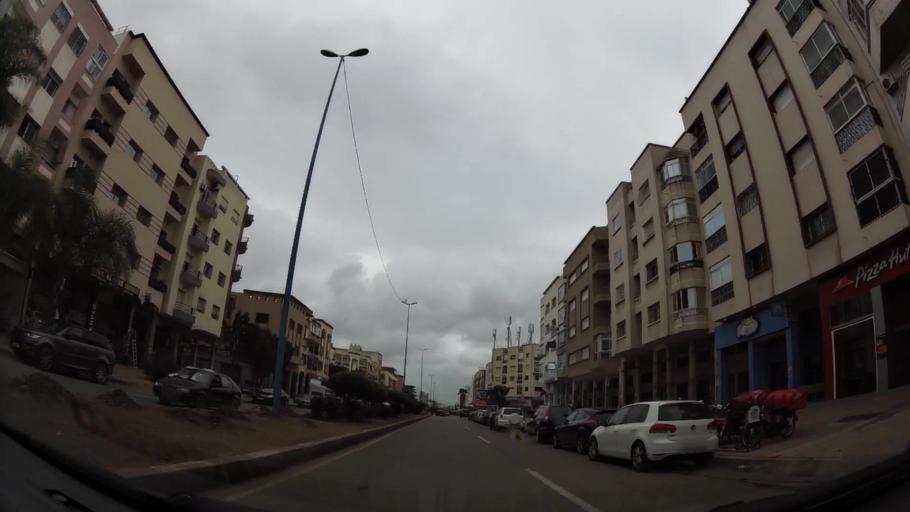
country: MA
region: Grand Casablanca
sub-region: Casablanca
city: Casablanca
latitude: 33.5328
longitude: -7.6151
